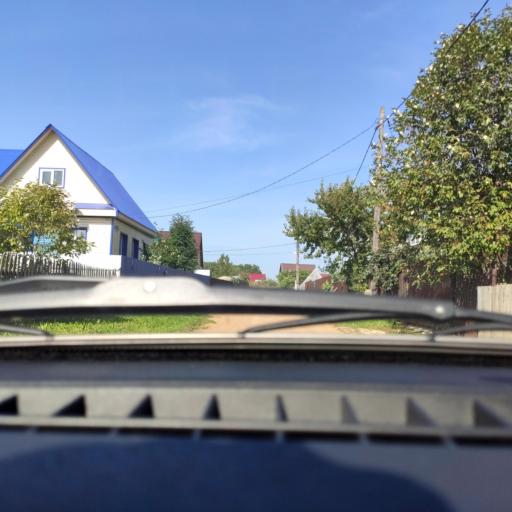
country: RU
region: Bashkortostan
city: Iglino
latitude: 54.8489
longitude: 56.4250
